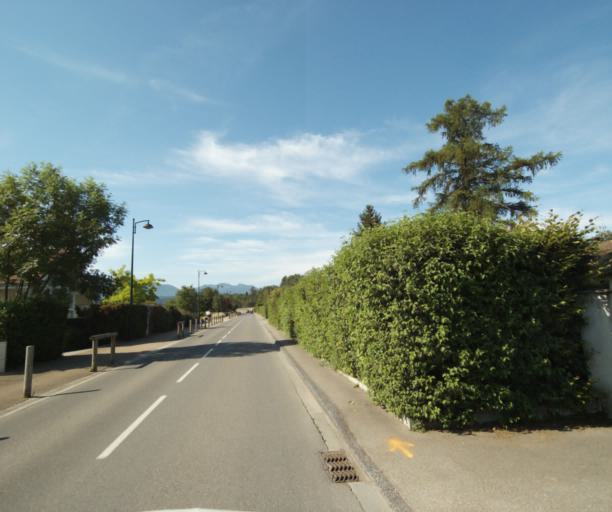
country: FR
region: Rhone-Alpes
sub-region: Departement de la Haute-Savoie
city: Marin
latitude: 46.3966
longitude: 6.5033
